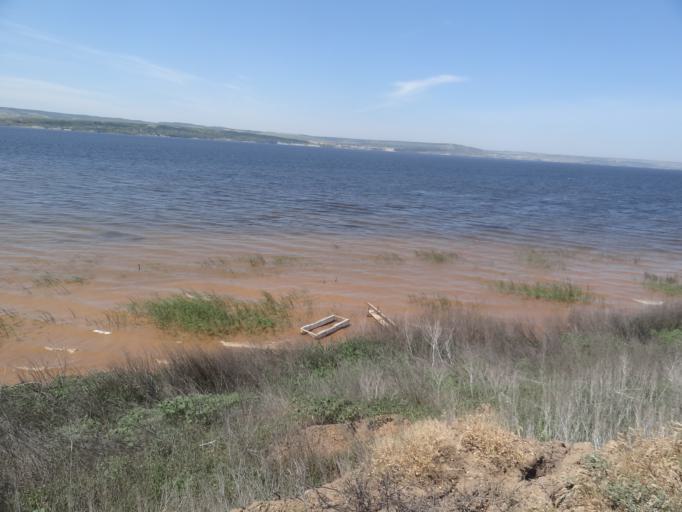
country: RU
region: Saratov
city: Krasnoarmeysk
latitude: 51.0932
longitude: 45.9393
